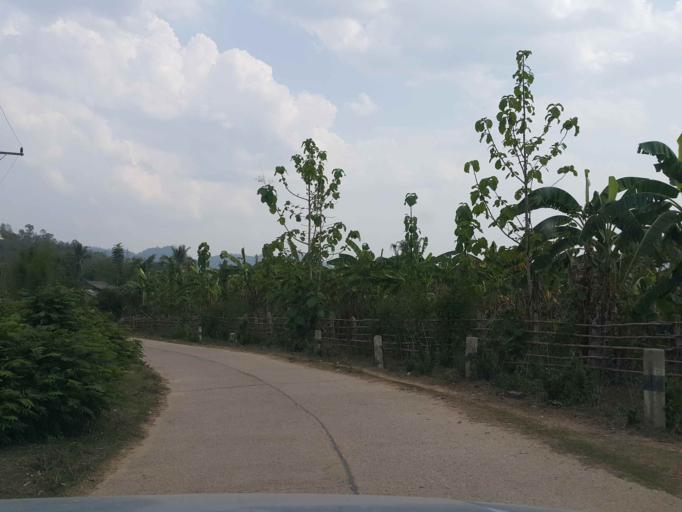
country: TH
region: Chiang Mai
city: Wiang Haeng
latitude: 19.4000
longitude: 98.7220
